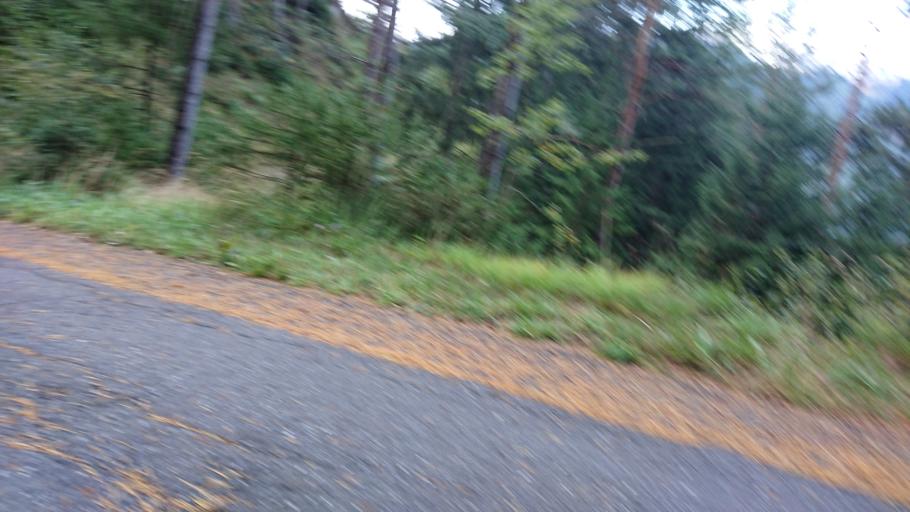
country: IT
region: Trentino-Alto Adige
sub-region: Bolzano
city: Campo di Trens
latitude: 46.8771
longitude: 11.4926
